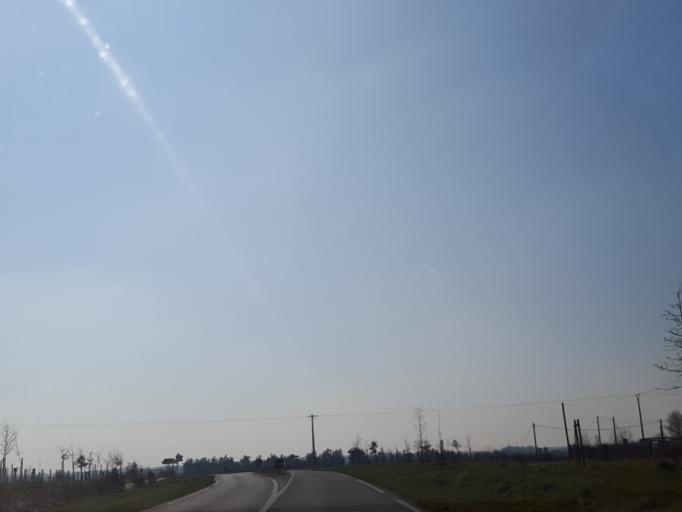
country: FR
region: Pays de la Loire
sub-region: Departement de la Vendee
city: Saint-Fulgent
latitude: 46.8566
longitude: -1.1915
